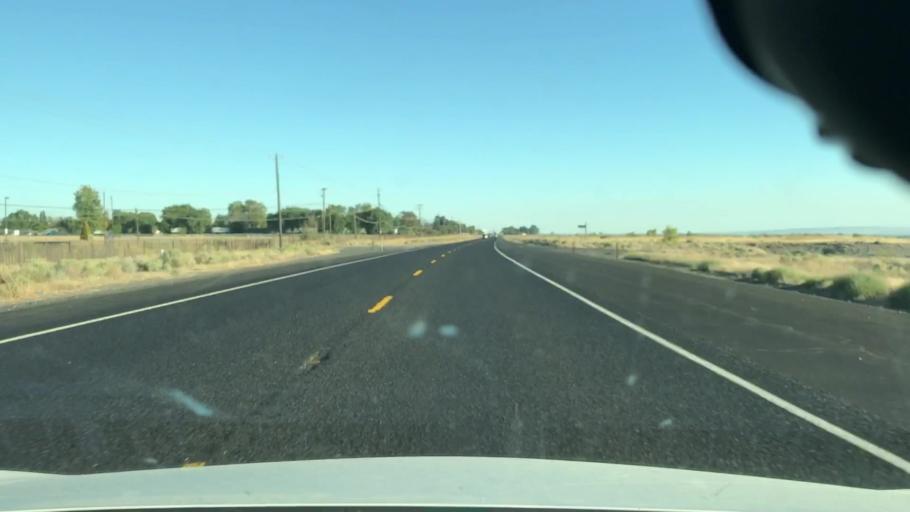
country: US
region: Washington
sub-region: Grant County
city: Moses Lake North
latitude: 47.1744
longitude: -119.3305
